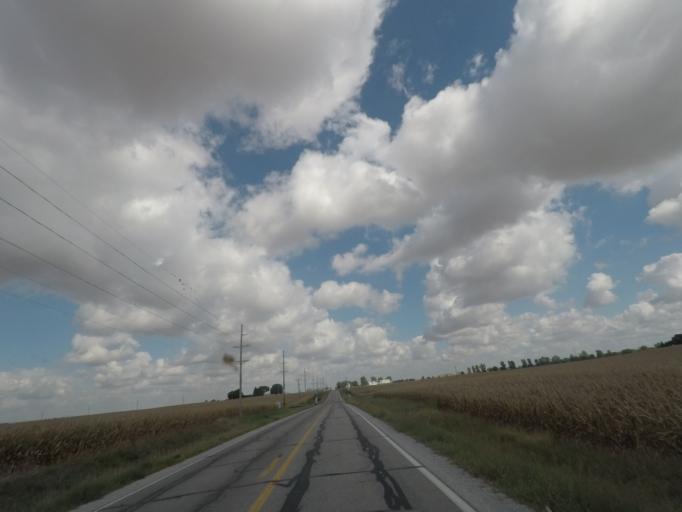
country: US
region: Iowa
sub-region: Story County
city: Nevada
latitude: 42.0182
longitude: -93.4057
